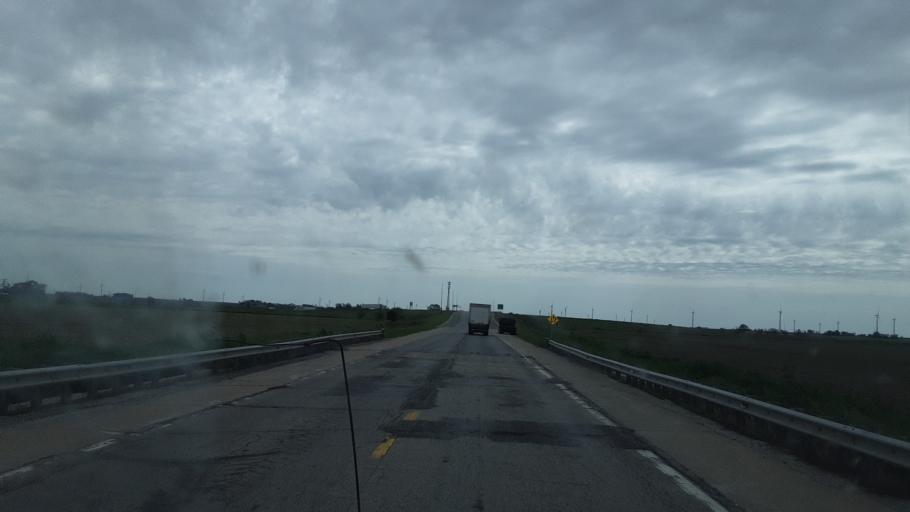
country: US
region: Illinois
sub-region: Tazewell County
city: Richmond
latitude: 40.3080
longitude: -89.4618
